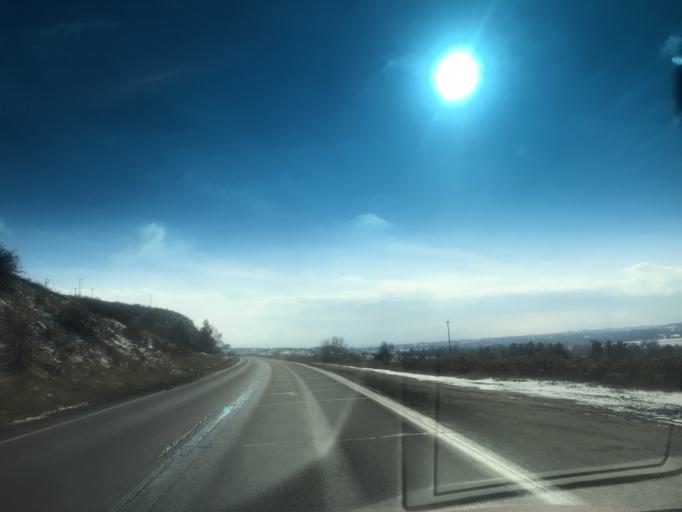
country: US
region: Colorado
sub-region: Douglas County
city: Castle Pines
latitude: 39.4591
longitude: -104.9841
